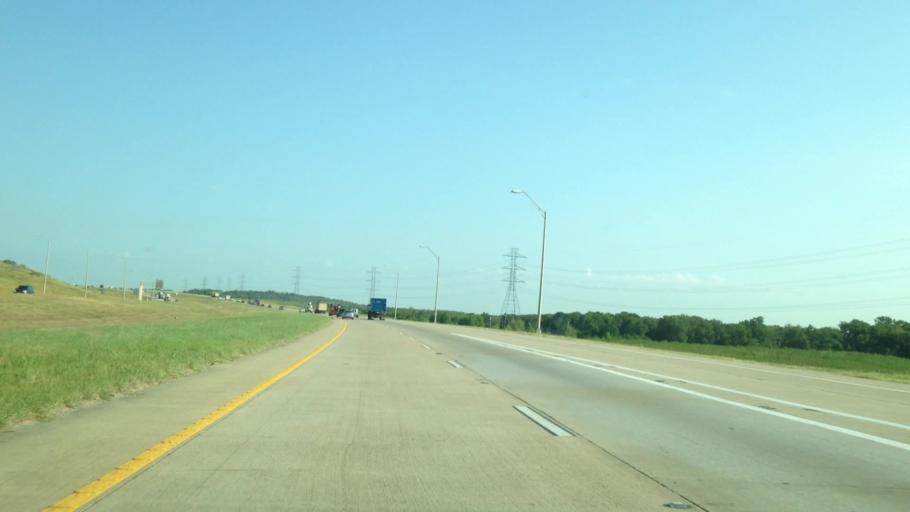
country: US
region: Texas
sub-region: Travis County
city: Manor
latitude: 30.3052
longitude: -97.5691
